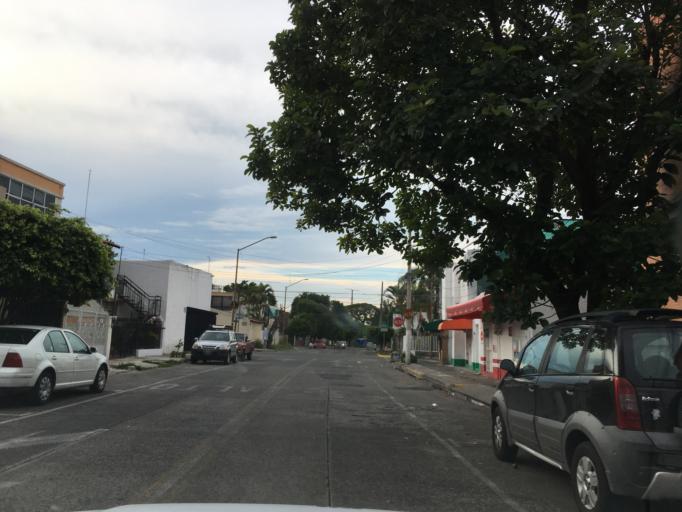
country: MX
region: Jalisco
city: Guadalajara
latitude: 20.6647
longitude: -103.3824
